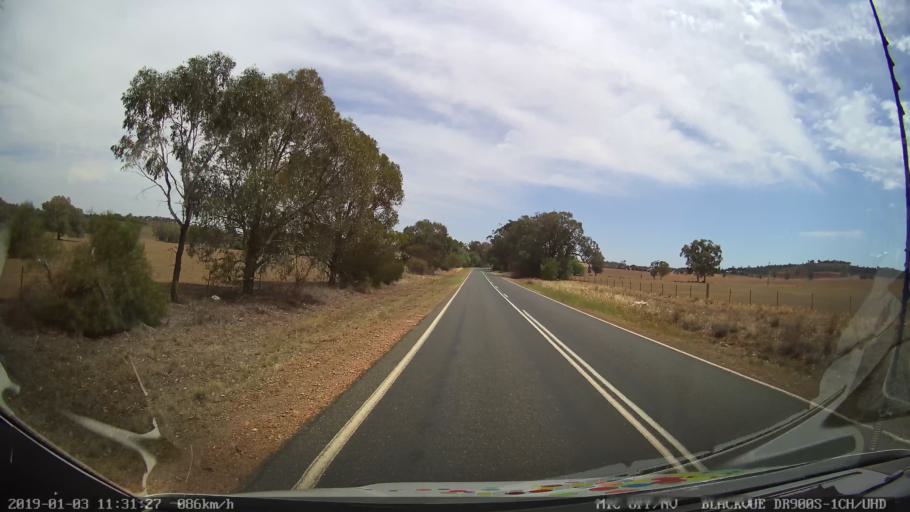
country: AU
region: New South Wales
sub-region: Weddin
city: Grenfell
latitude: -33.9704
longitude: 148.1834
